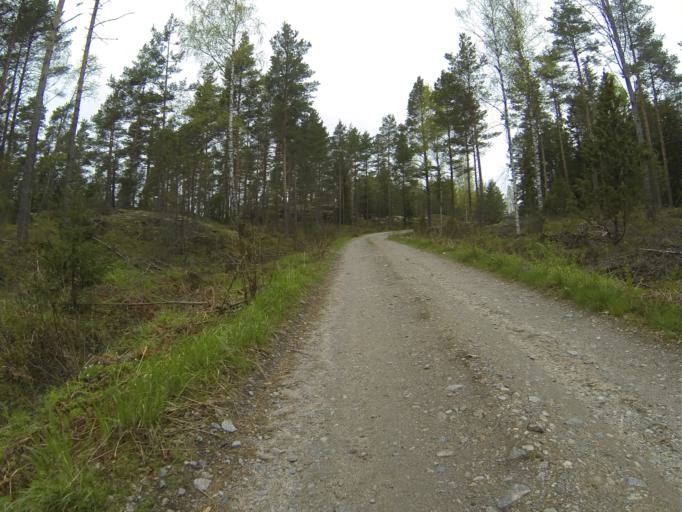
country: FI
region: Varsinais-Suomi
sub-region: Salo
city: Pertteli
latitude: 60.3826
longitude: 23.2175
